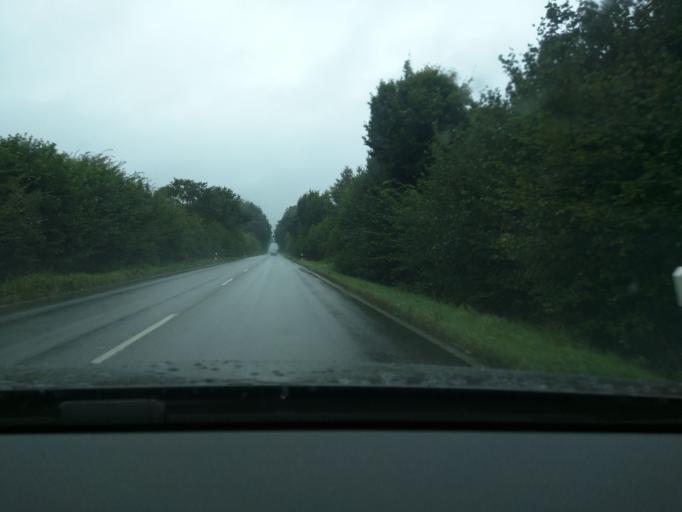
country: DE
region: Schleswig-Holstein
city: Wangelau
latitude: 53.4586
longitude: 10.5478
